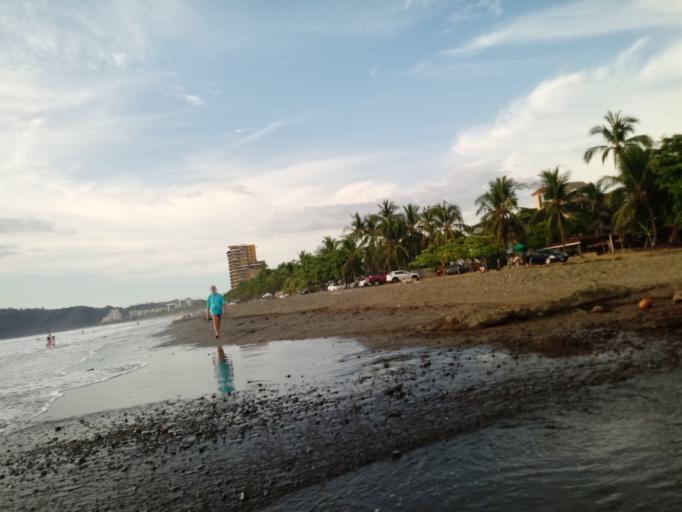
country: CR
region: Puntarenas
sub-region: Canton de Garabito
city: Jaco
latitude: 9.6060
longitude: -84.6239
